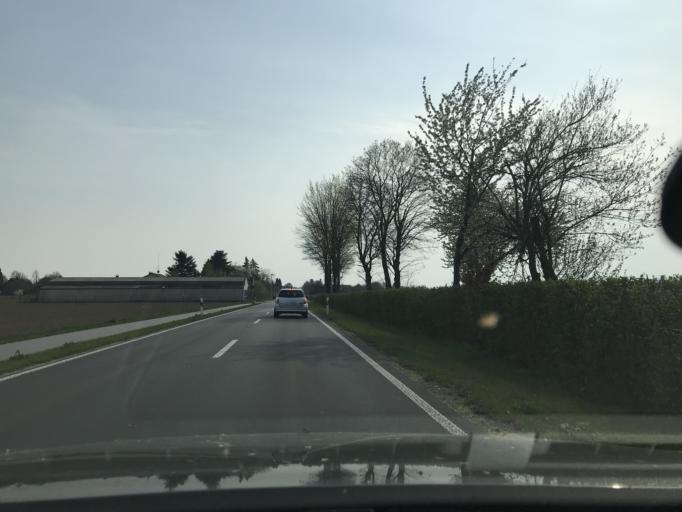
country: DE
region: North Rhine-Westphalia
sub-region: Regierungsbezirk Dusseldorf
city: Goch
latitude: 51.7247
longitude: 6.1663
